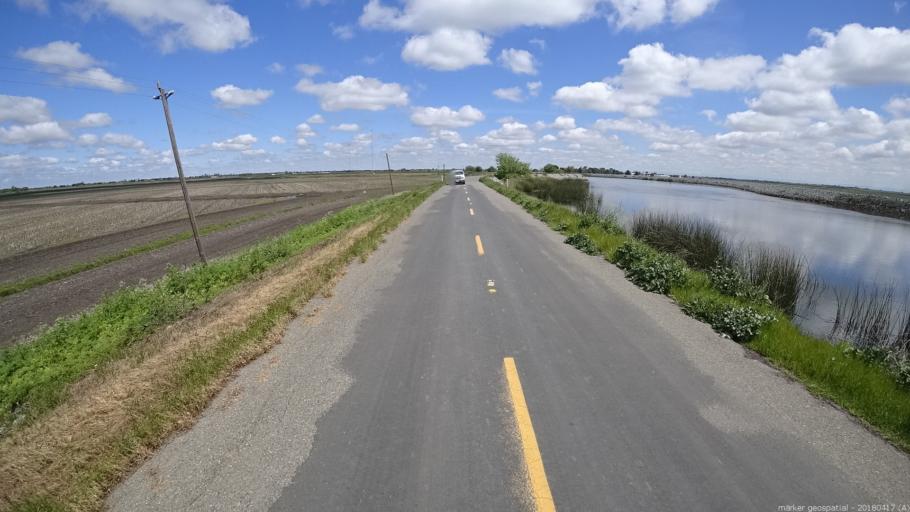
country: US
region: California
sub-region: Sacramento County
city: Walnut Grove
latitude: 38.1963
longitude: -121.5288
